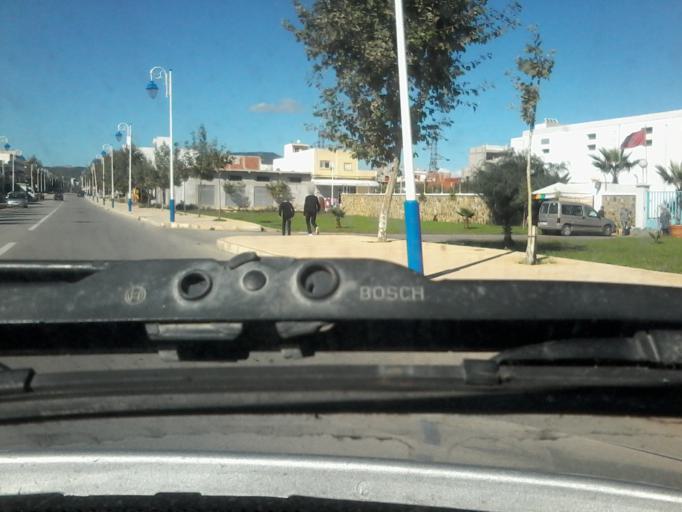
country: MA
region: Tanger-Tetouan
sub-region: Tetouan
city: Martil
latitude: 35.6961
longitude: -5.3451
